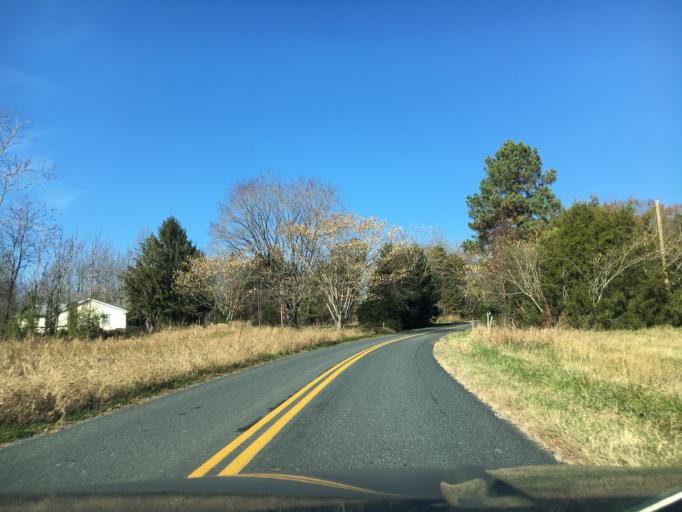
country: US
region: Virginia
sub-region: Buckingham County
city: Buckingham
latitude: 37.4260
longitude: -78.6145
